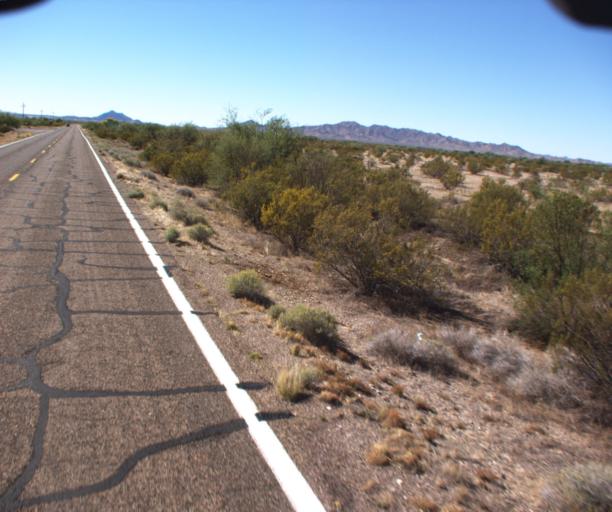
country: US
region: Arizona
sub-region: Pima County
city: Ajo
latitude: 32.4673
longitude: -112.8750
